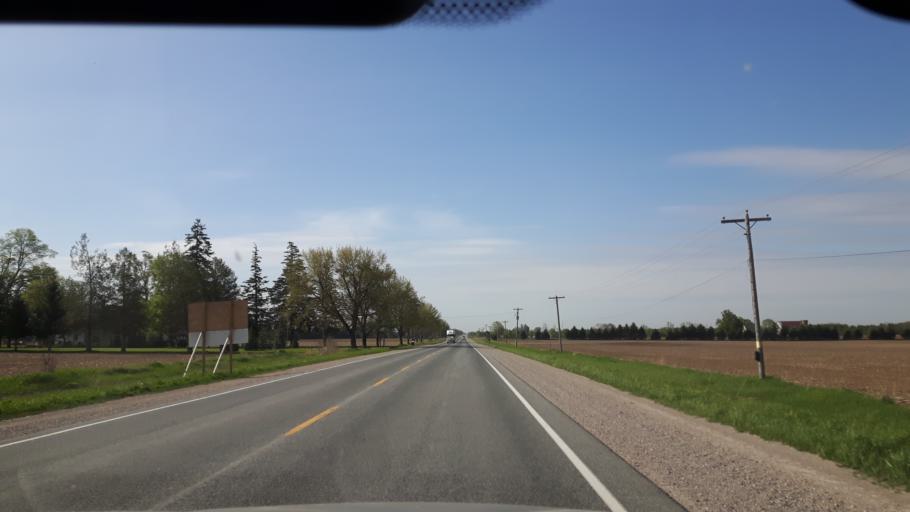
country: CA
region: Ontario
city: Bluewater
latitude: 43.5184
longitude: -81.5159
